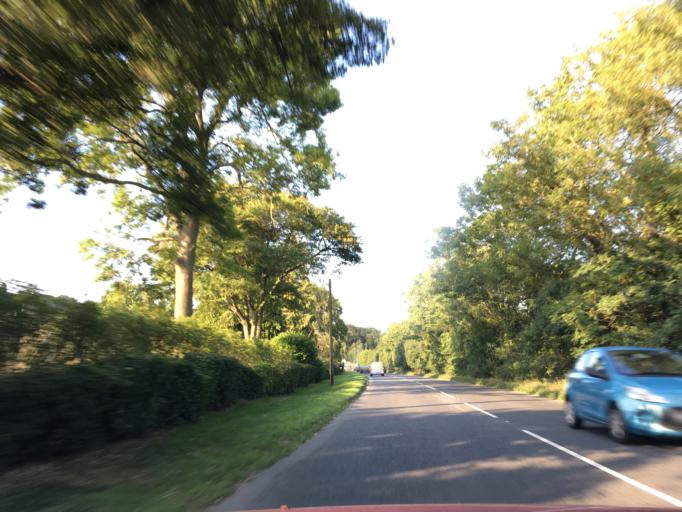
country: GB
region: England
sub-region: Gloucestershire
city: Stow on the Wold
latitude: 51.9147
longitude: -1.7279
